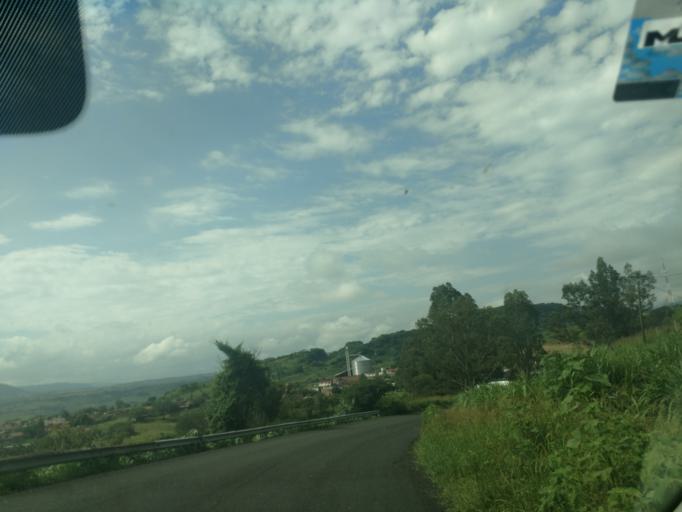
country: MX
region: Jalisco
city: El Salto
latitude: 20.4243
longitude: -104.4980
